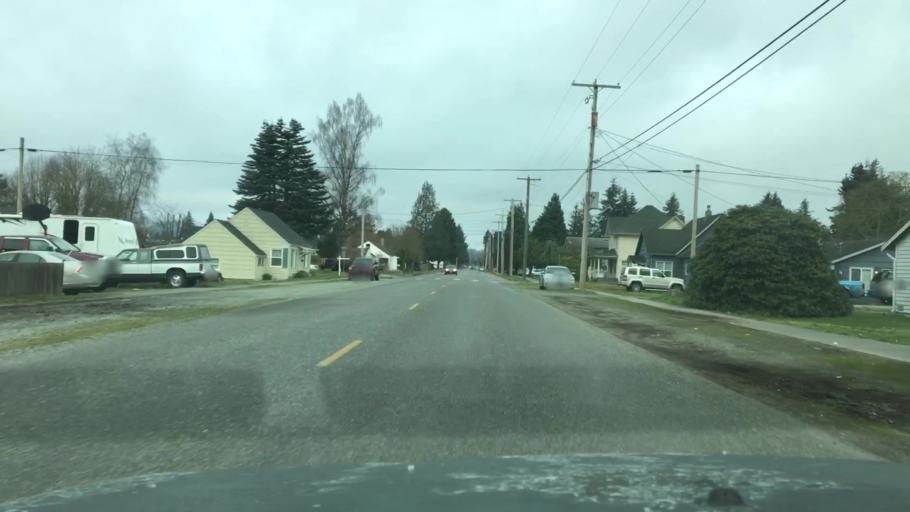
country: US
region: Washington
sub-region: Skagit County
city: Sedro-Woolley
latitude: 48.4963
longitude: -122.2260
